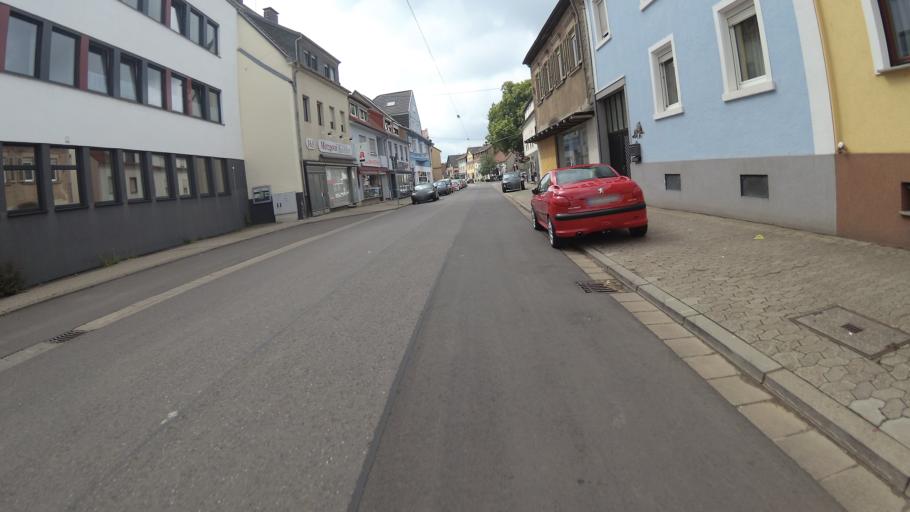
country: FR
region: Lorraine
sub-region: Departement de la Moselle
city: Alsting
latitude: 49.2007
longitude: 7.0279
